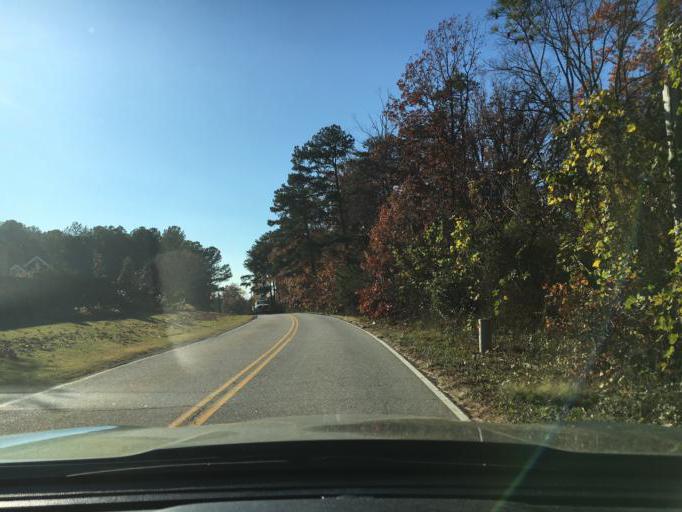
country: US
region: South Carolina
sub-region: Spartanburg County
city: Inman Mills
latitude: 35.0534
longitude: -82.1298
